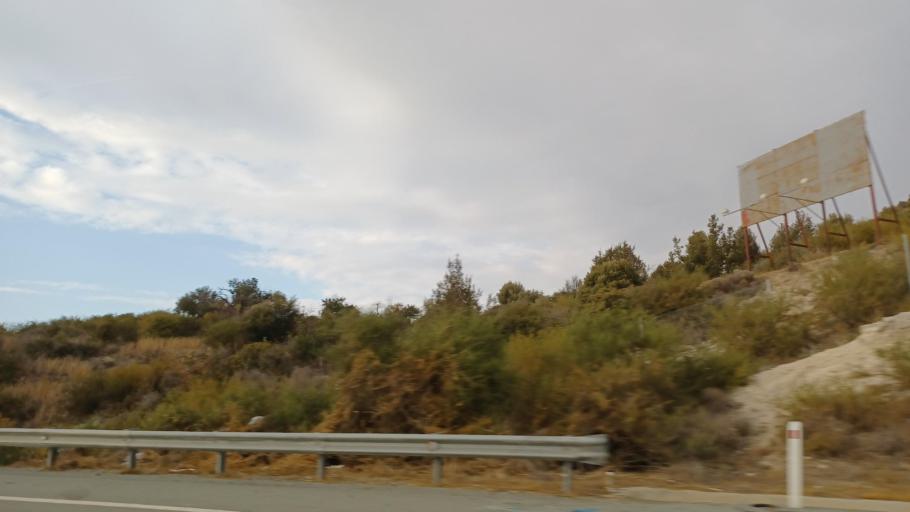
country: CY
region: Limassol
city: Pissouri
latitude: 34.6842
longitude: 32.7045
